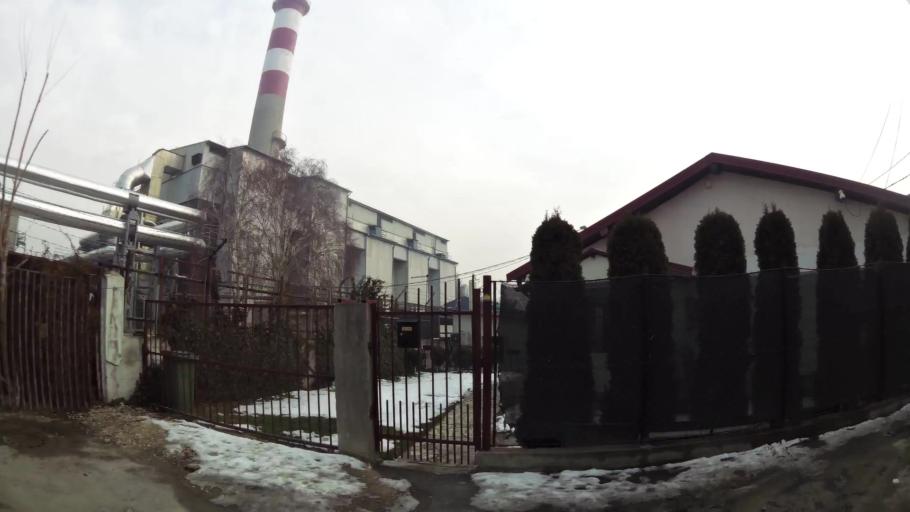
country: MK
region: Karpos
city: Skopje
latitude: 41.9935
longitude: 21.4529
